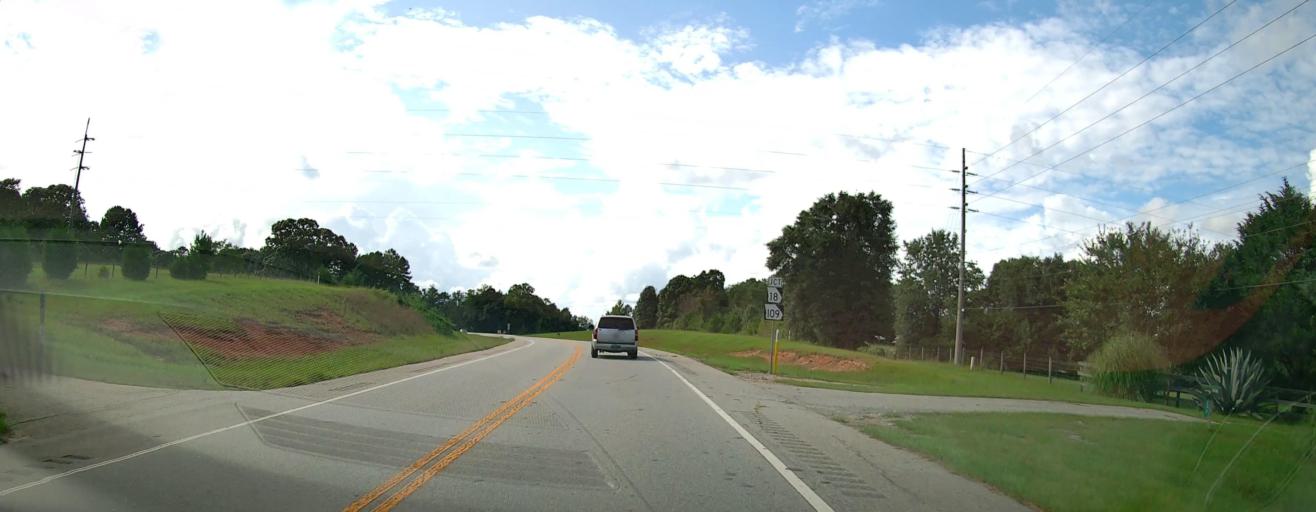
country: US
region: Georgia
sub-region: Upson County
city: Hannahs Mill
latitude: 32.9912
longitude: -84.5054
